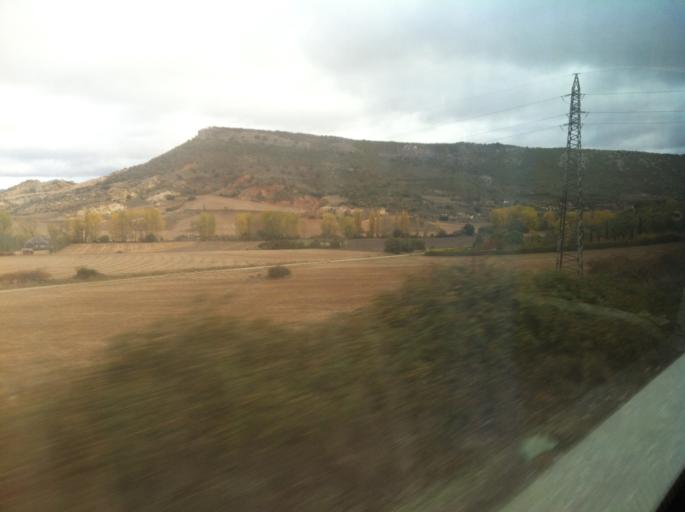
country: ES
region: Castille and Leon
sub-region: Provincia de Burgos
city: Bugedo
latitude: 42.6494
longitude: -3.0132
